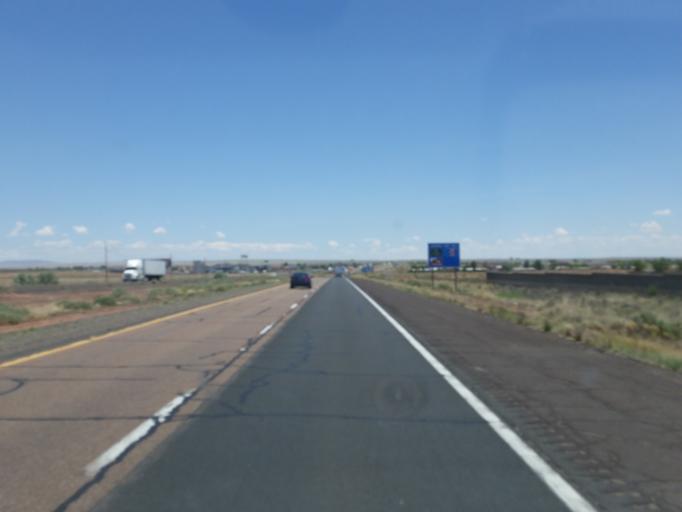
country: US
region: Arizona
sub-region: Navajo County
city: Winslow
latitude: 35.0383
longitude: -110.7156
